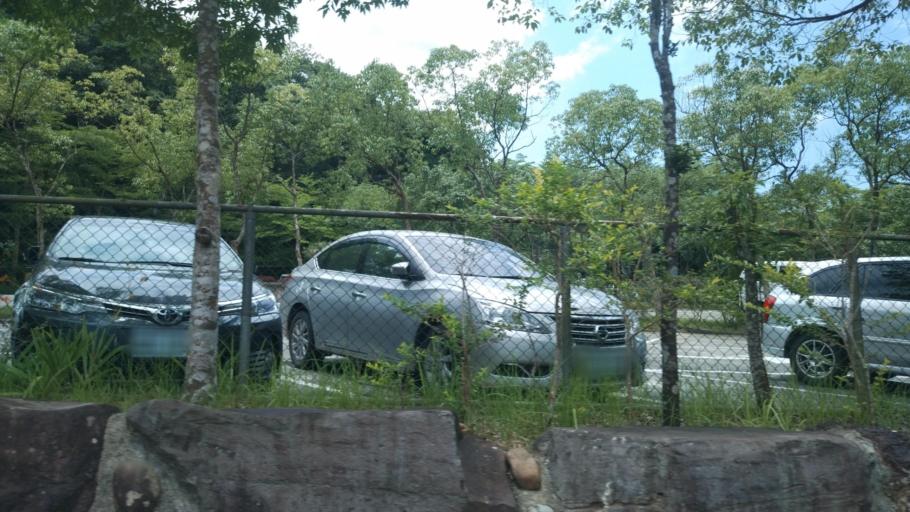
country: TW
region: Taipei
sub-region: Taipei
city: Banqiao
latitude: 24.9200
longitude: 121.4254
